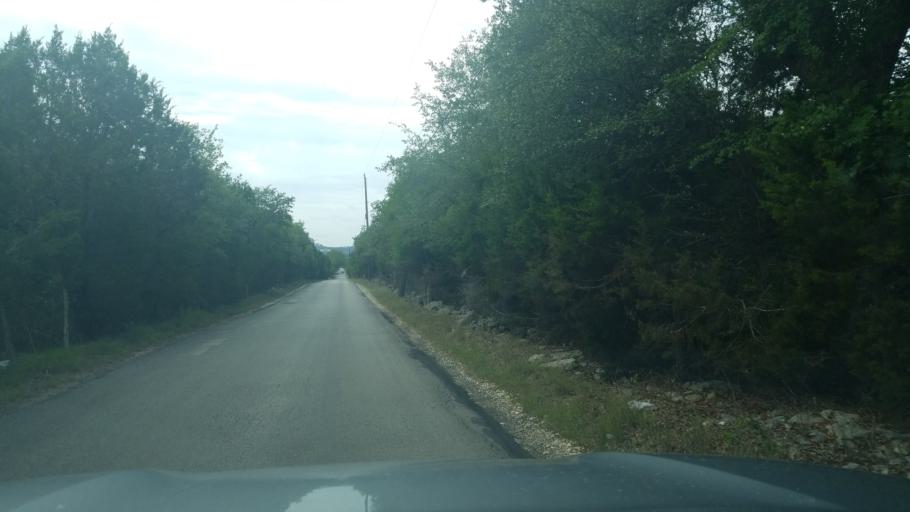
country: US
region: Texas
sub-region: Comal County
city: Bulverde
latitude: 29.7552
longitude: -98.4111
